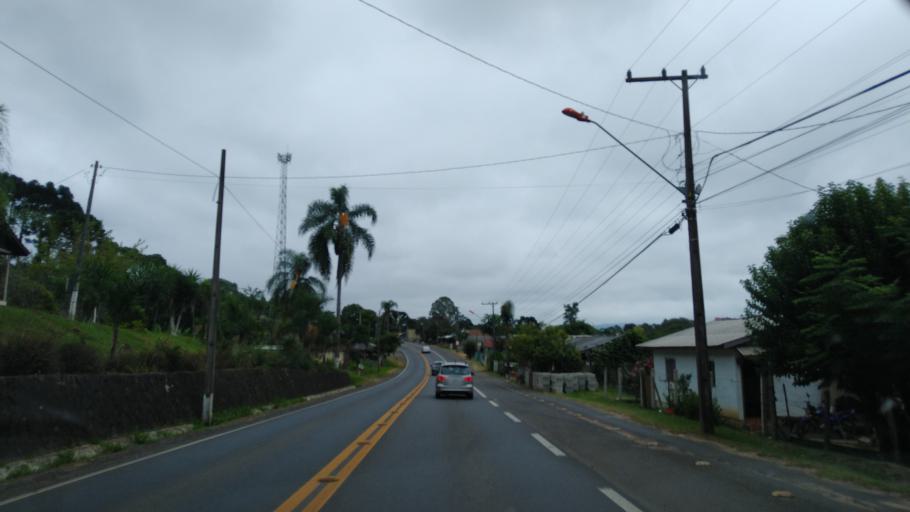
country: BR
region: Santa Catarina
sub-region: Porto Uniao
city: Porto Uniao
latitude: -26.2726
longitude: -51.0549
